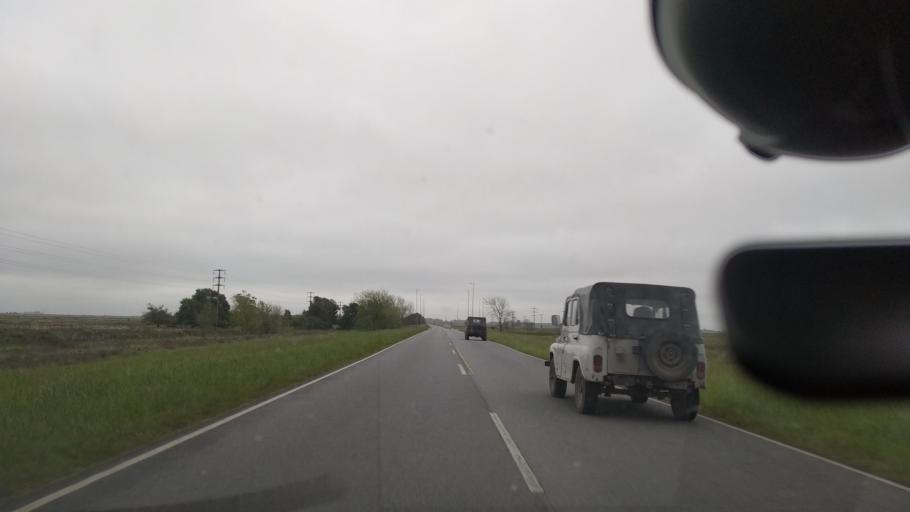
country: AR
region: Buenos Aires
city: Veronica
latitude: -35.3639
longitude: -57.3965
